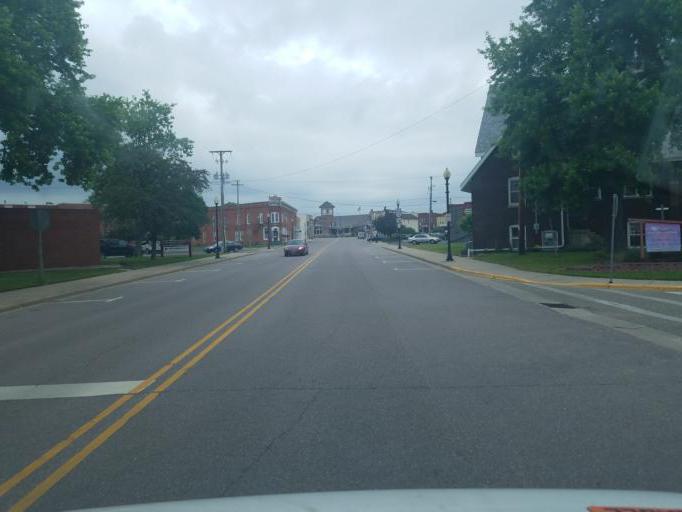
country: US
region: Wisconsin
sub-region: Juneau County
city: Mauston
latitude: 43.7954
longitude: -90.0771
